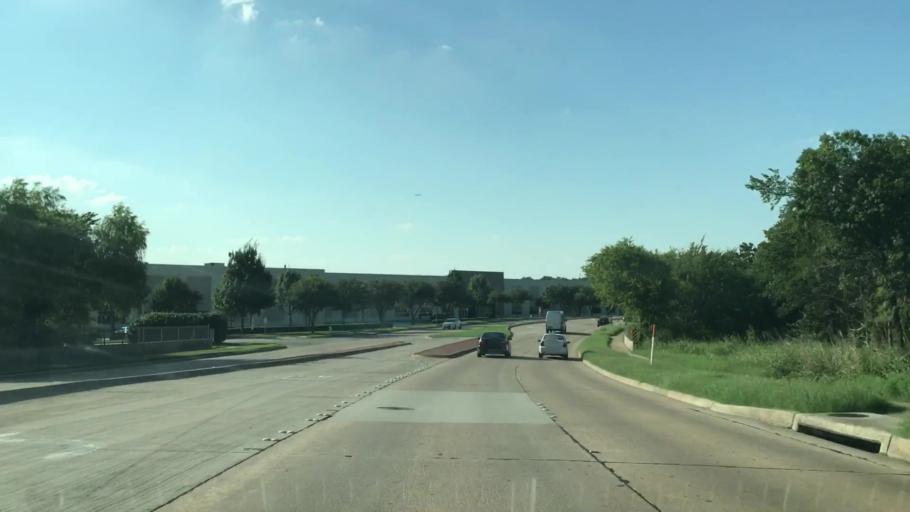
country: US
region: Texas
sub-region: Dallas County
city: Coppell
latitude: 32.9956
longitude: -97.0052
